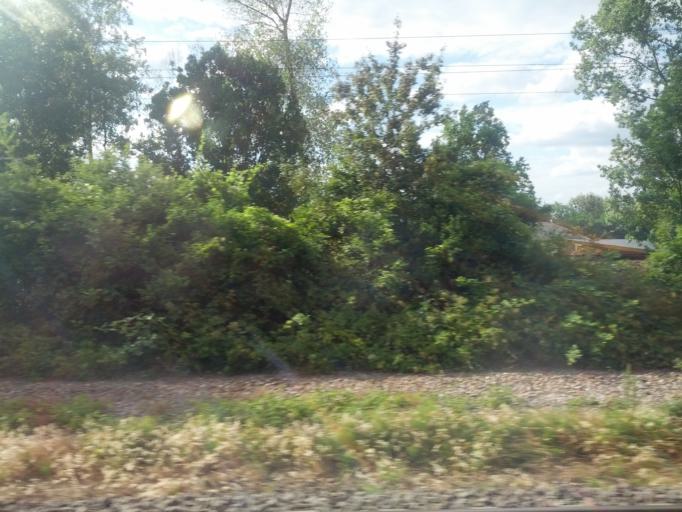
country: DE
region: Baden-Wuerttemberg
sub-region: Karlsruhe Region
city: Karlsruhe
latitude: 49.0045
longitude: 8.4683
